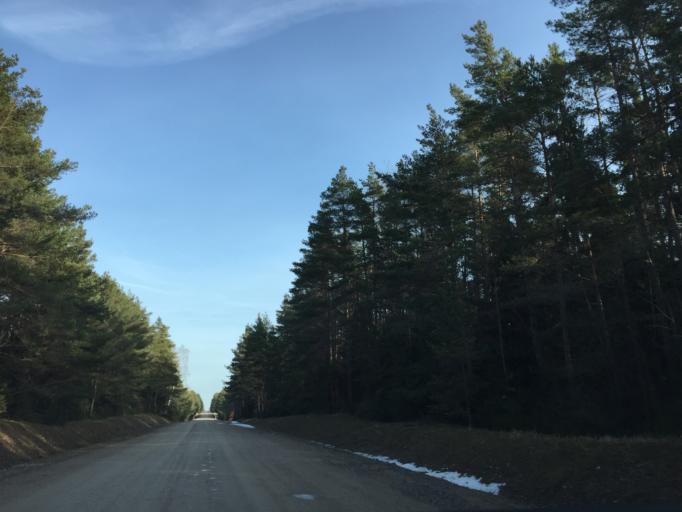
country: EE
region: Saare
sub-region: Kuressaare linn
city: Kuressaare
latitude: 58.3105
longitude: 21.9780
